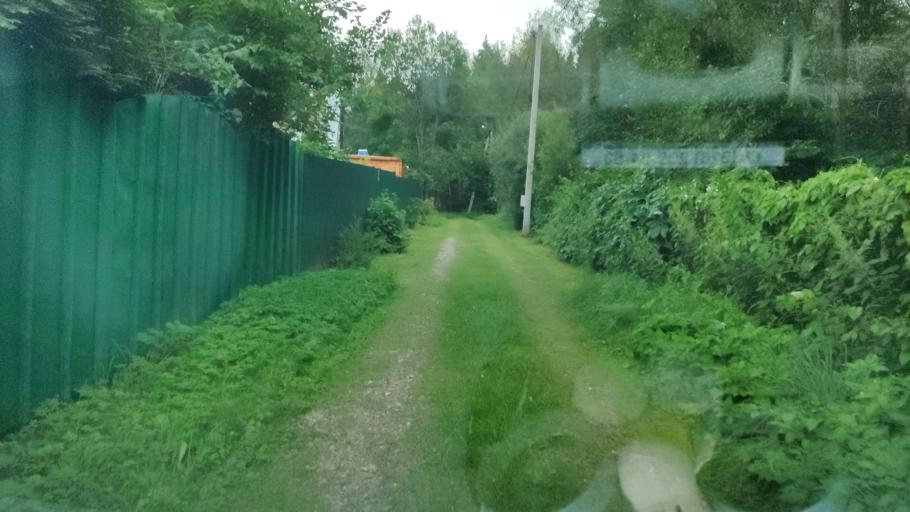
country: RU
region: Moskovskaya
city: Ashukino
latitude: 56.2088
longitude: 37.9784
